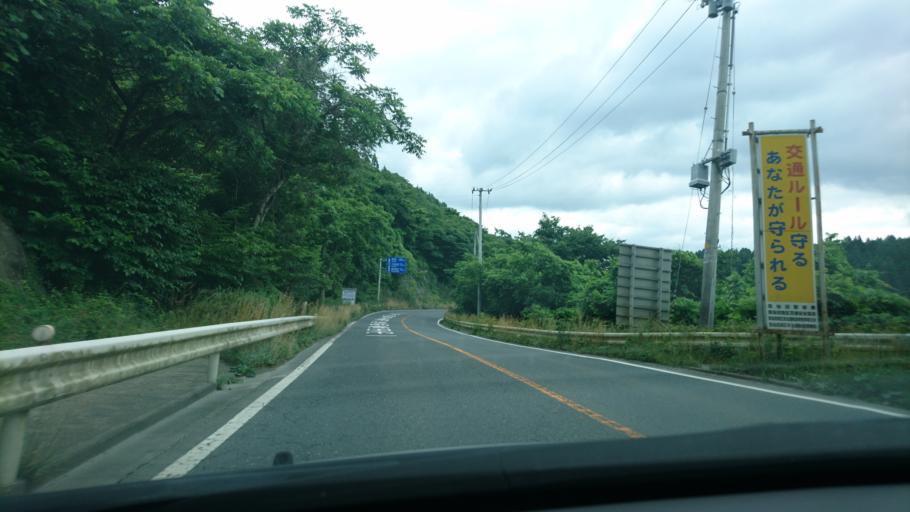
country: JP
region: Iwate
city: Ofunato
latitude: 38.9701
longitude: 141.6311
